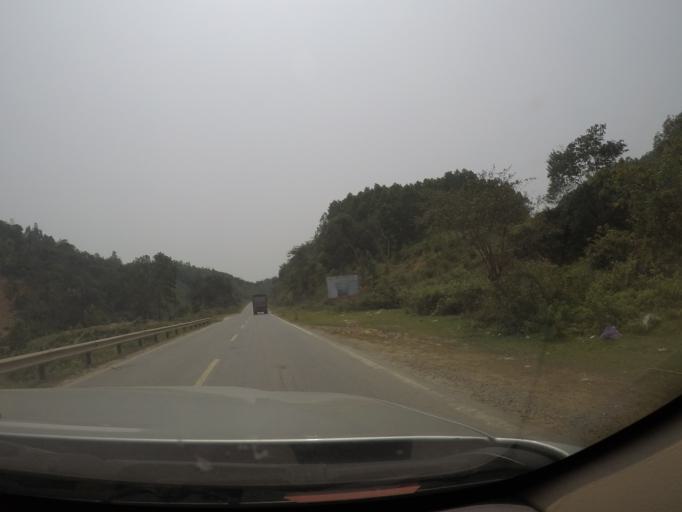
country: VN
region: Thanh Hoa
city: Thi Tran Yen Cat
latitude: 19.6730
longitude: 105.4541
